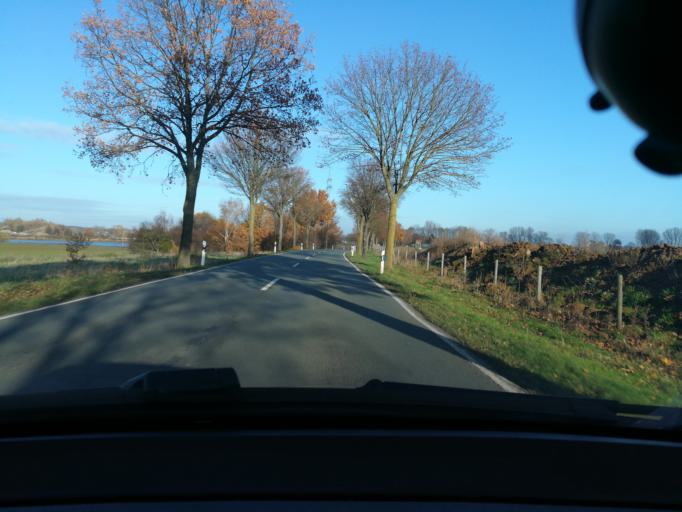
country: DE
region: North Rhine-Westphalia
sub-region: Regierungsbezirk Detmold
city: Minden
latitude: 52.3223
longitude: 8.9438
